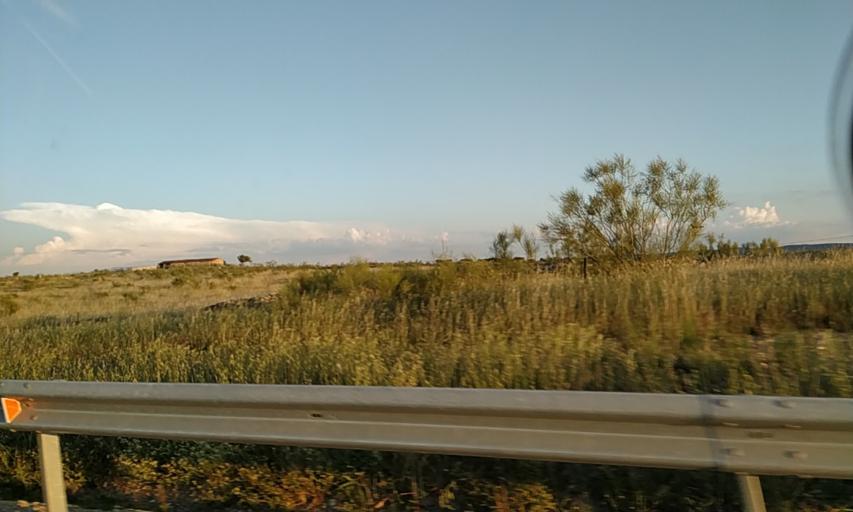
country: ES
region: Extremadura
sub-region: Provincia de Caceres
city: Salorino
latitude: 39.5145
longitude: -7.0558
